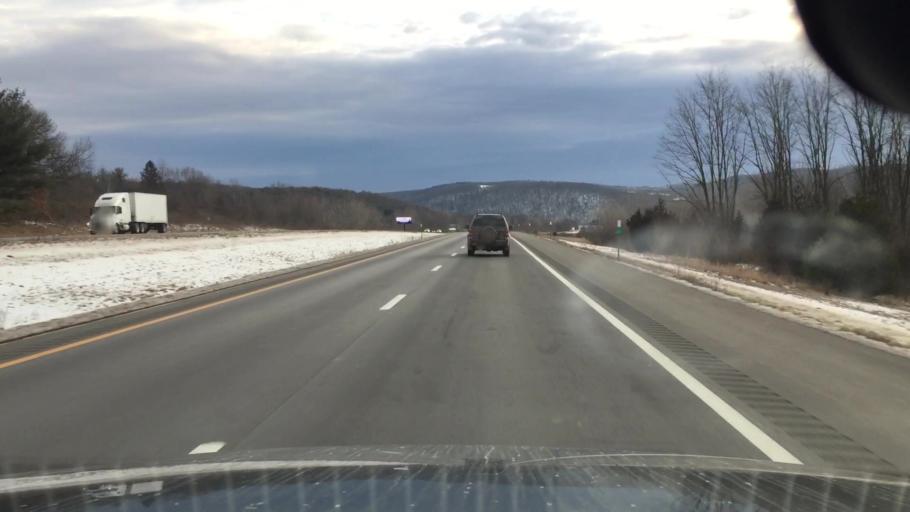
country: US
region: Pennsylvania
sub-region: Bradford County
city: Sayre
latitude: 42.0049
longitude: -76.4917
